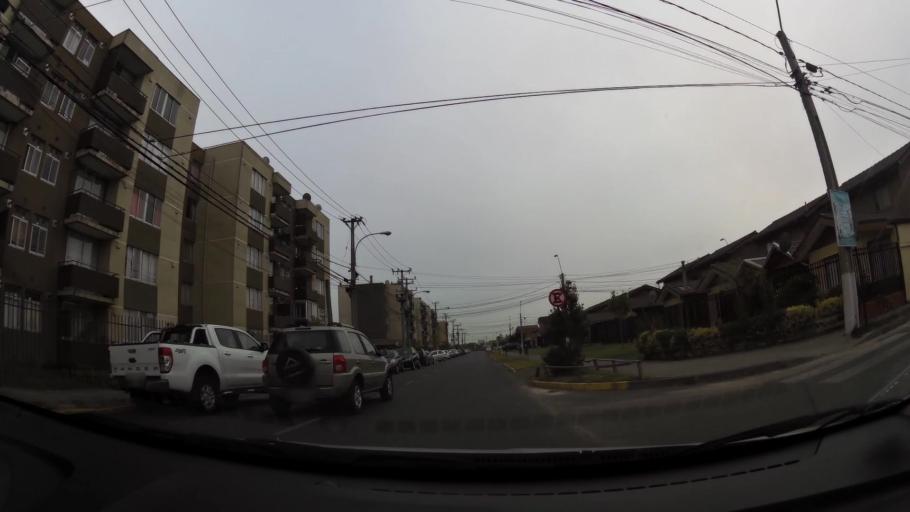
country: CL
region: Biobio
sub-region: Provincia de Concepcion
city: Concepcion
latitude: -36.7877
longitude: -73.0807
